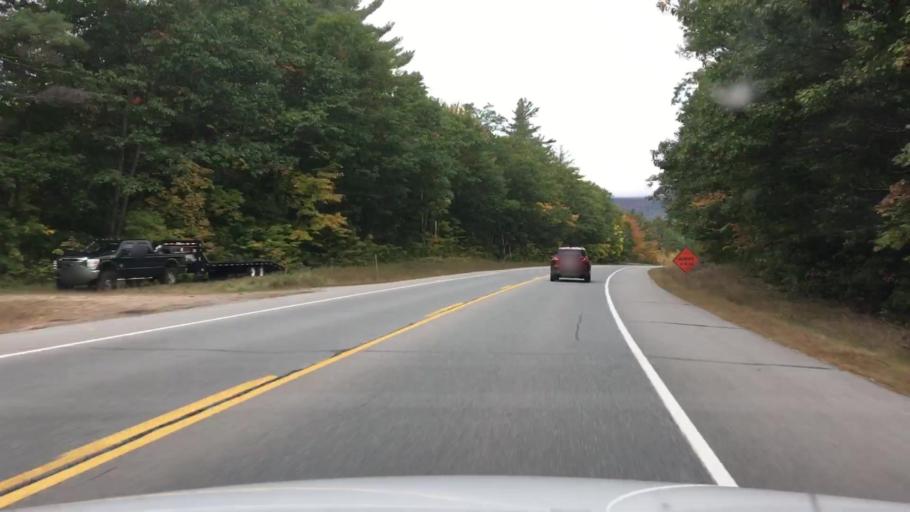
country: US
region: New Hampshire
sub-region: Coos County
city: Gorham
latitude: 44.3895
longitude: -71.0309
